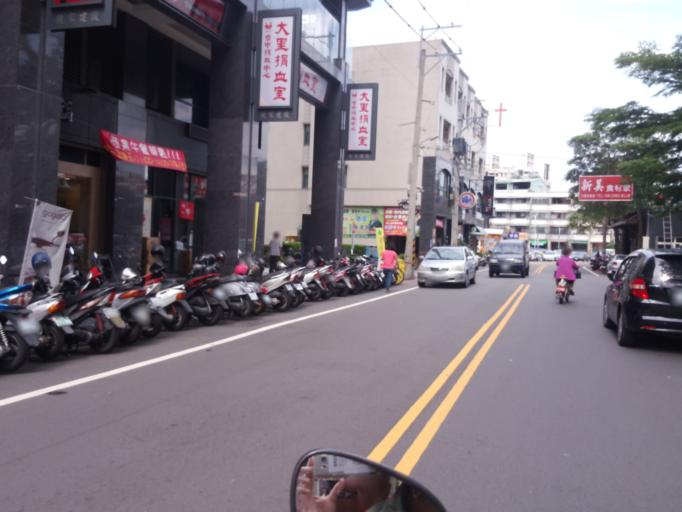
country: TW
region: Taiwan
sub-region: Taichung City
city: Taichung
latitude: 24.1100
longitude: 120.6905
